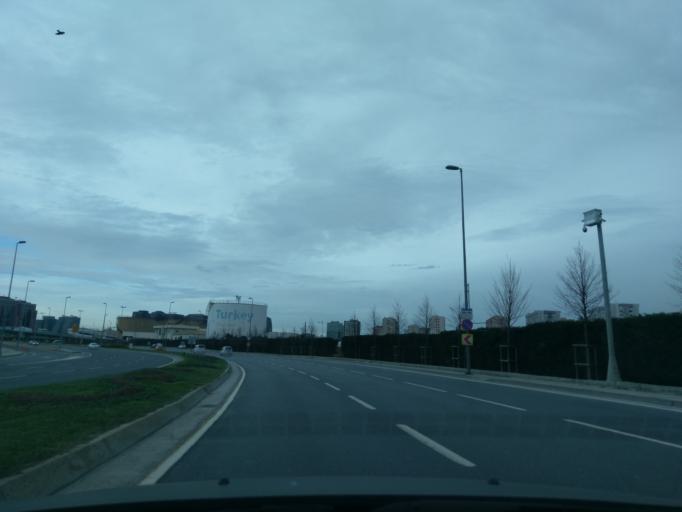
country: TR
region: Istanbul
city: Bahcelievler
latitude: 40.9804
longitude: 28.8408
